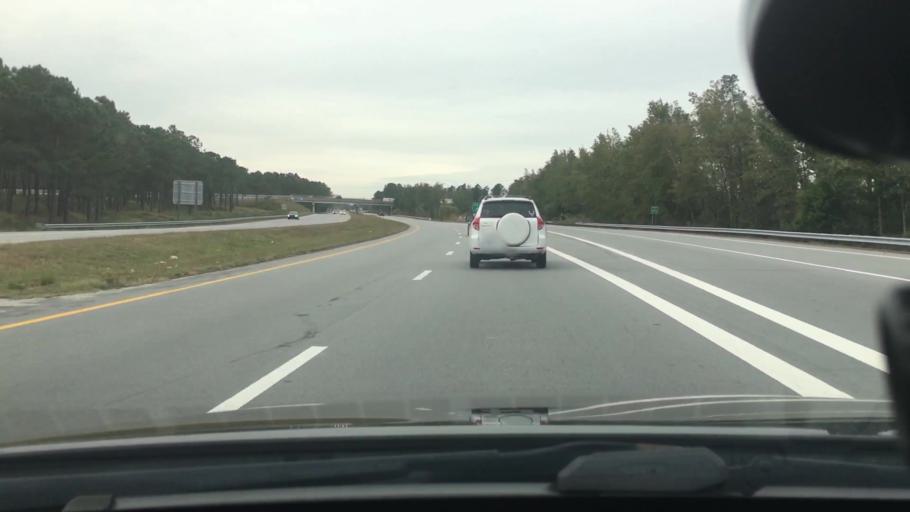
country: US
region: North Carolina
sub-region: Craven County
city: James City
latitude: 35.1117
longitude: -77.0095
